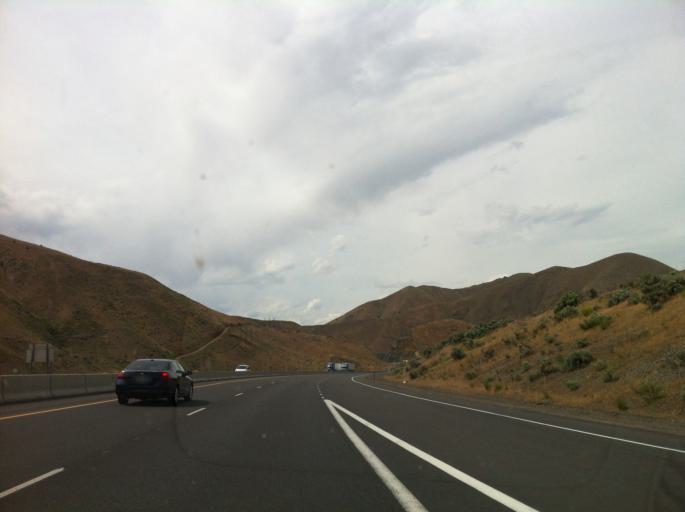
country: US
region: Idaho
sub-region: Washington County
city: Weiser
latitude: 44.4317
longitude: -117.3181
